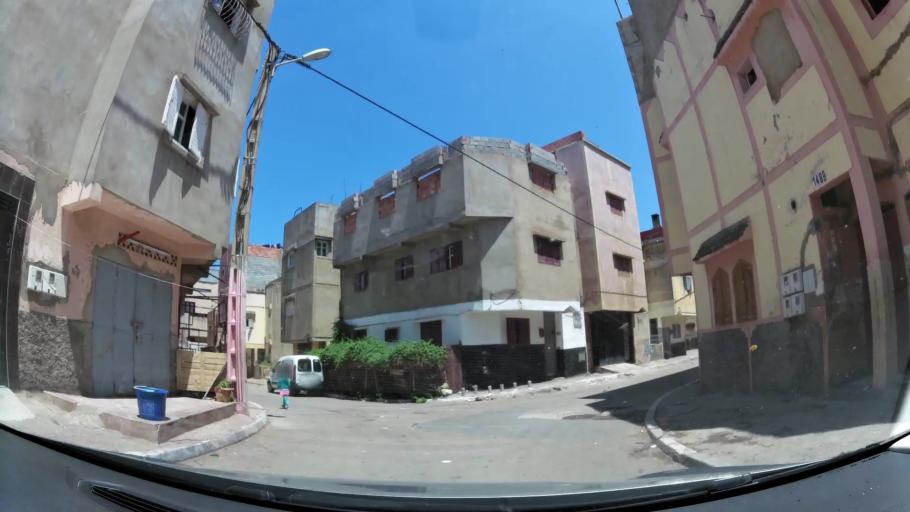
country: MA
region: Rabat-Sale-Zemmour-Zaer
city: Sale
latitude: 34.0708
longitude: -6.7861
